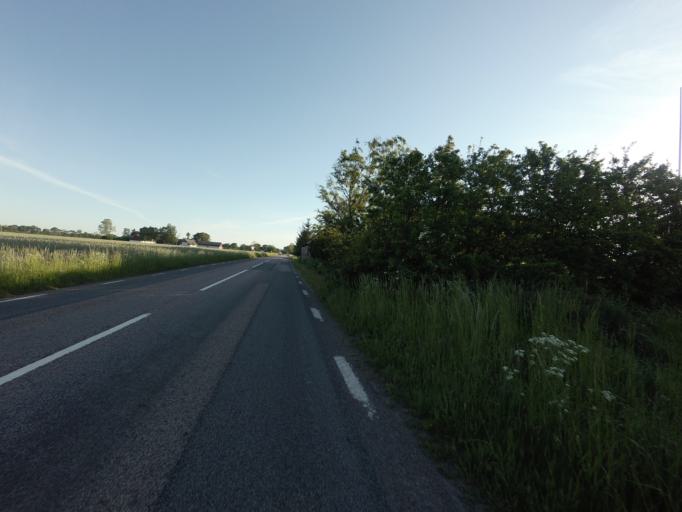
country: SE
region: Skane
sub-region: Helsingborg
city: Odakra
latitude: 56.1998
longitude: 12.6745
